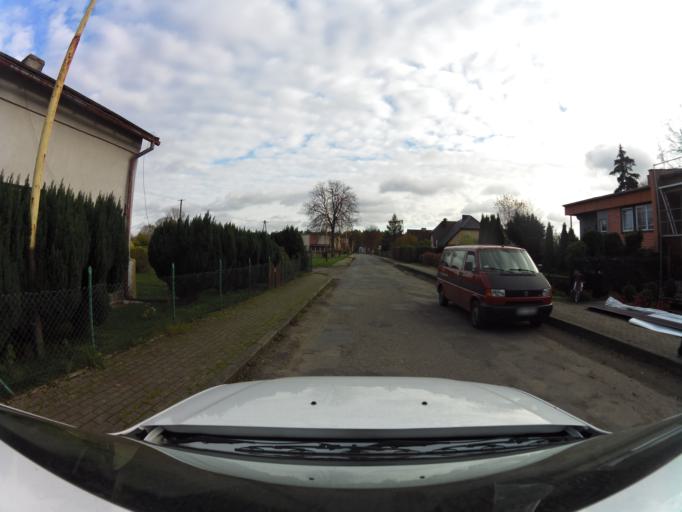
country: PL
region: West Pomeranian Voivodeship
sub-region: Powiat gryficki
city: Gryfice
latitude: 53.9535
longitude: 15.1924
